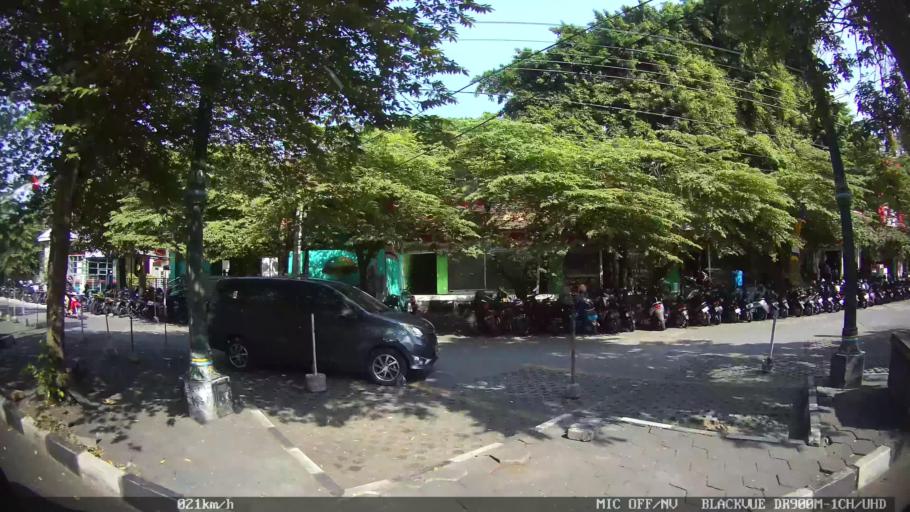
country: ID
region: Daerah Istimewa Yogyakarta
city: Yogyakarta
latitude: -7.8006
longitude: 110.3683
